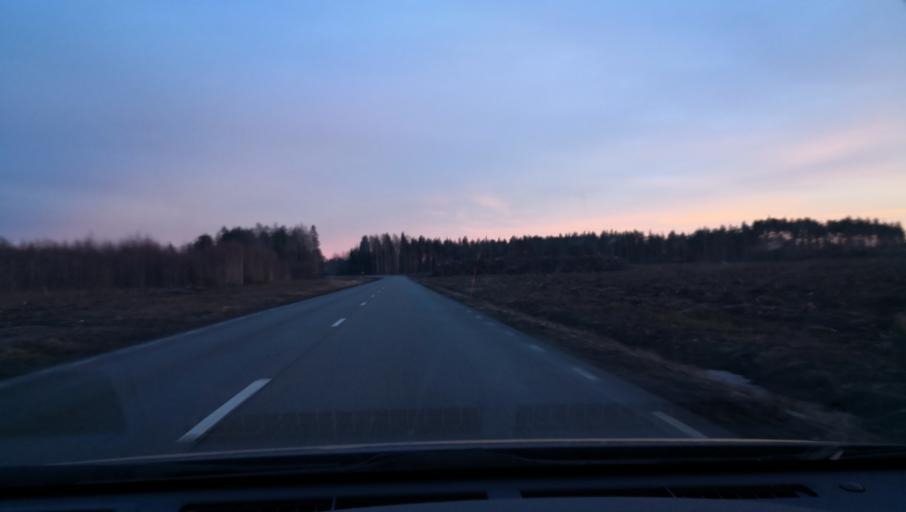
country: SE
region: OErebro
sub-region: Orebro Kommun
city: Orebro
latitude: 59.2372
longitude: 15.1105
